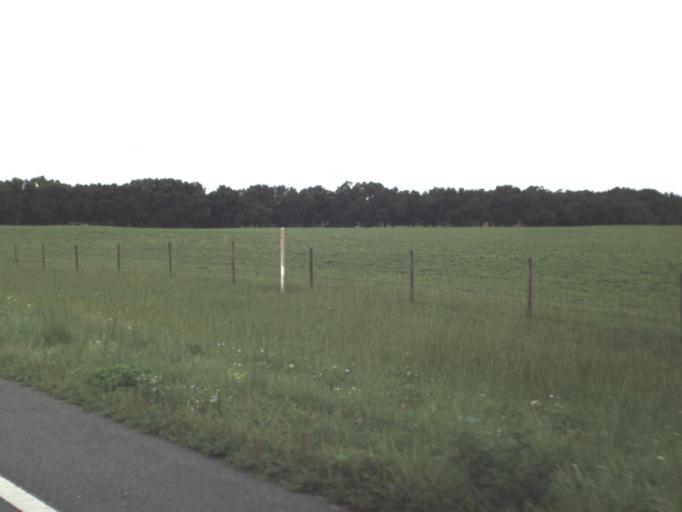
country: US
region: Florida
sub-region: Levy County
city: Williston Highlands
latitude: 29.2564
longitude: -82.4416
